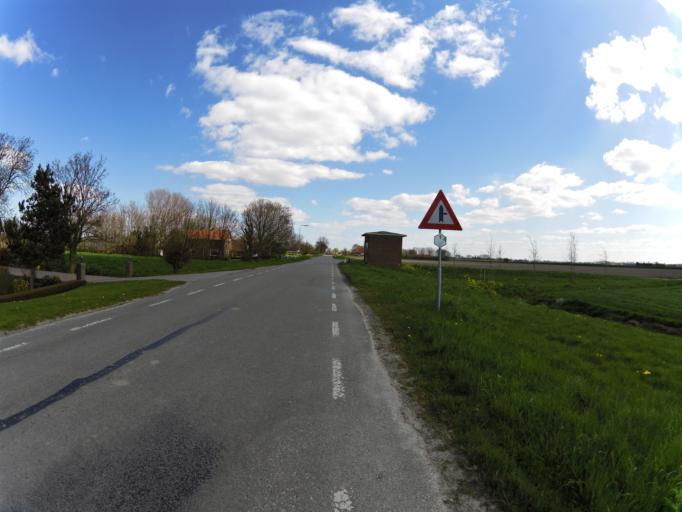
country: NL
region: South Holland
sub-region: Gemeente Hellevoetsluis
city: Nieuwenhoorn
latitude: 51.8807
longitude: 4.1278
